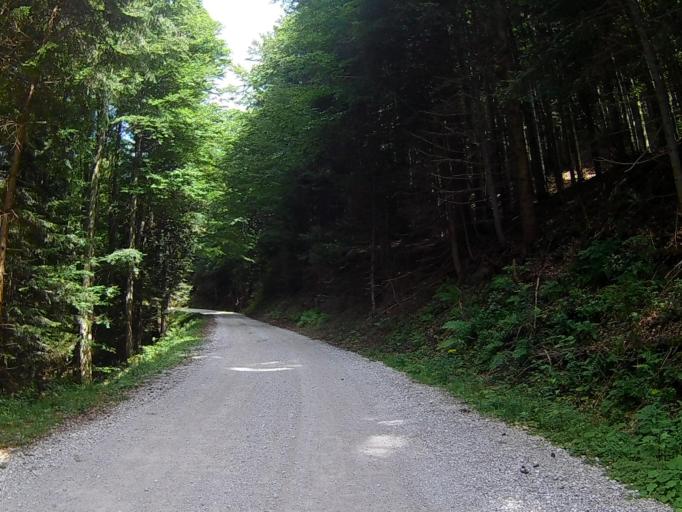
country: SI
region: Selnica ob Dravi
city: Selnica ob Dravi
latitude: 46.4898
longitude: 15.4633
